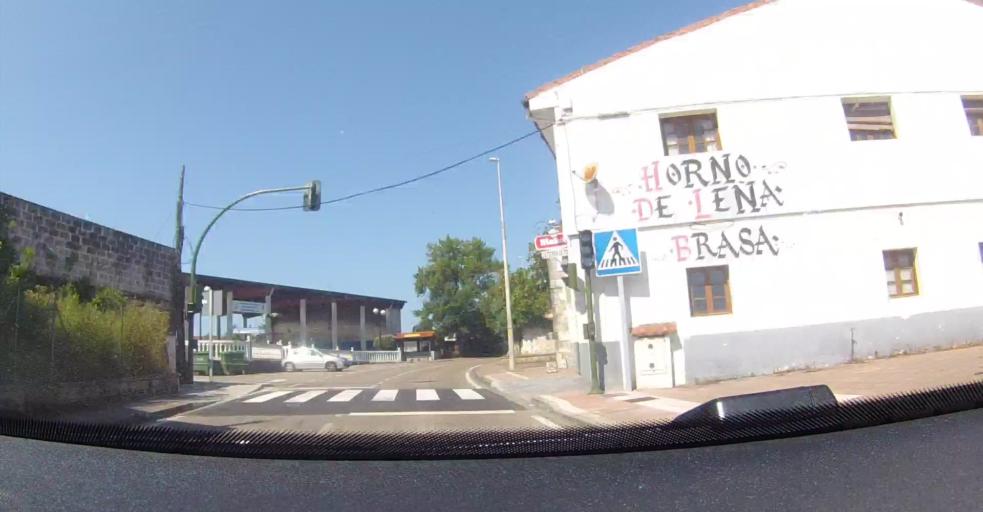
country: ES
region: Cantabria
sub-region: Provincia de Cantabria
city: Argonos
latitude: 43.4568
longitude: -3.4930
